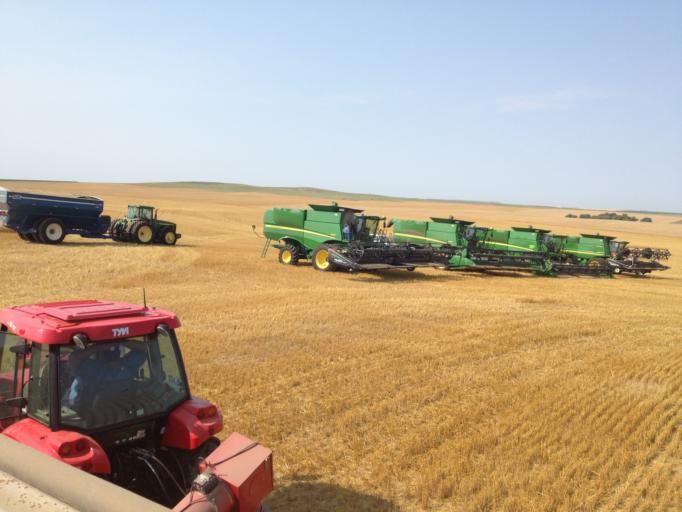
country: US
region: North Dakota
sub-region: Adams County
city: Hettinger
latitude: 45.9057
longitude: -102.9372
